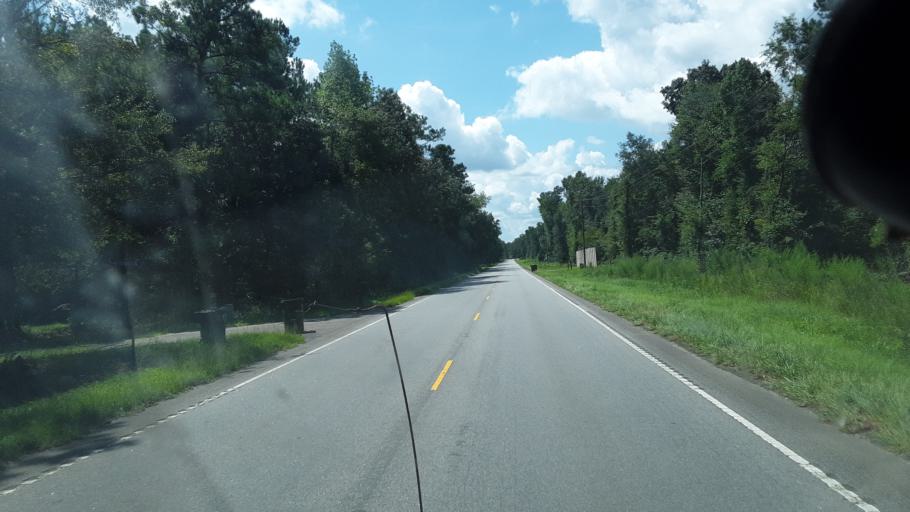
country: US
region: South Carolina
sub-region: Berkeley County
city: Moncks Corner
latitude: 33.2485
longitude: -79.9382
